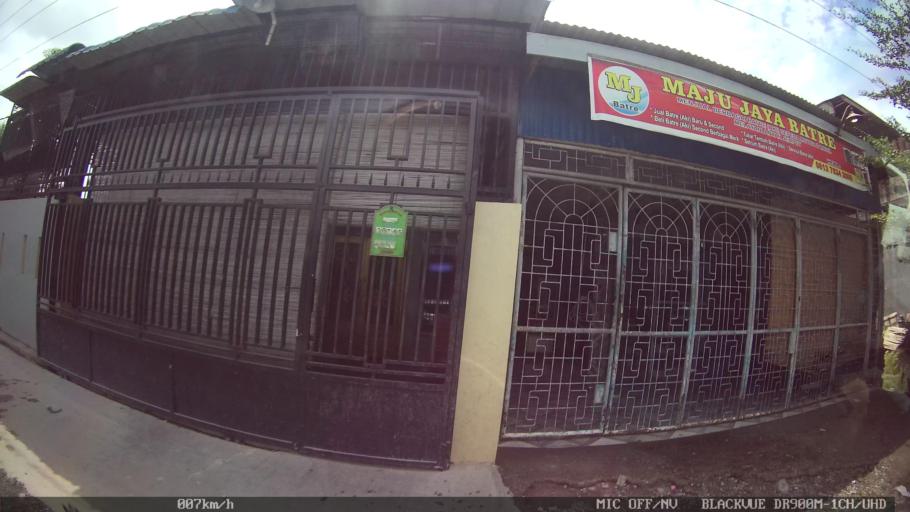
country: ID
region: North Sumatra
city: Medan
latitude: 3.6121
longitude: 98.7611
